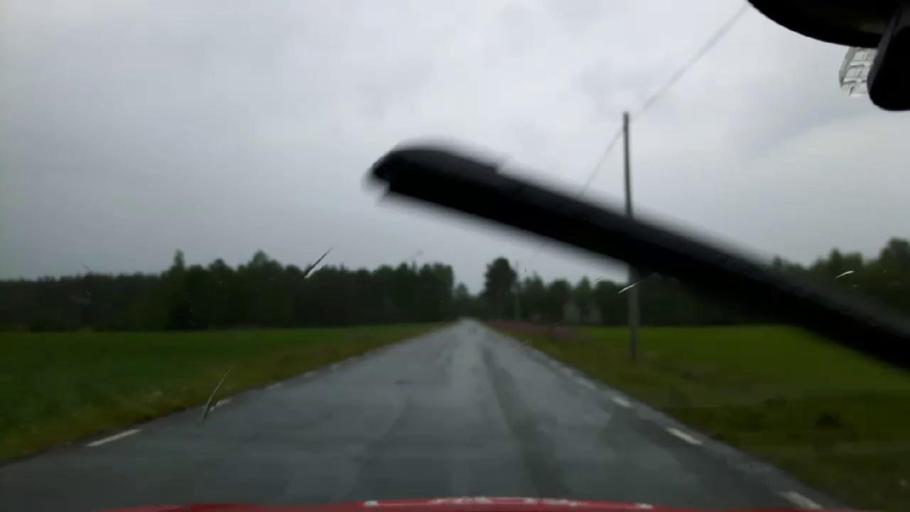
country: SE
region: Jaemtland
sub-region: OEstersunds Kommun
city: Brunflo
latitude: 62.9916
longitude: 14.7946
